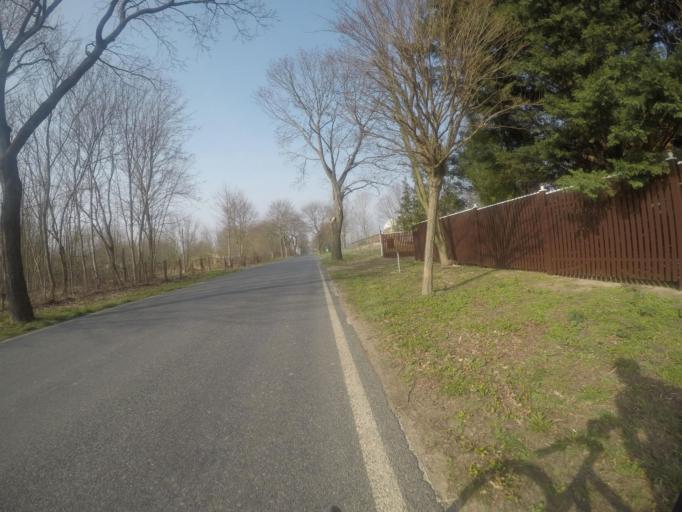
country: DE
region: Brandenburg
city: Mittenwalde
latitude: 52.3120
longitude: 13.5116
